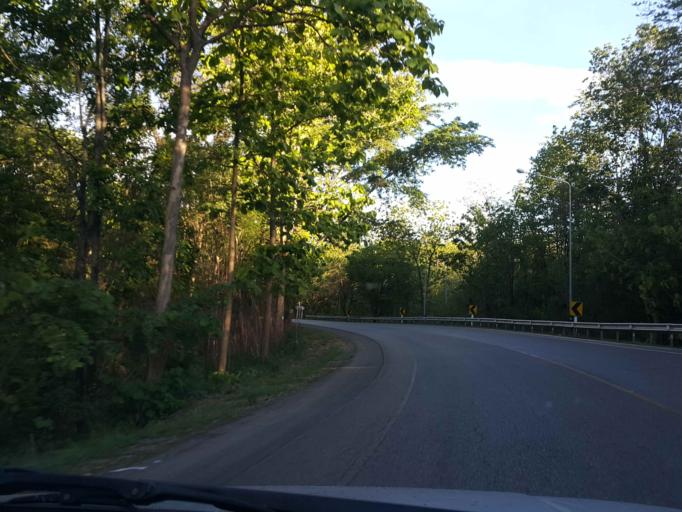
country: TH
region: Chiang Mai
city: Chom Thong
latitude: 18.4752
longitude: 98.6760
